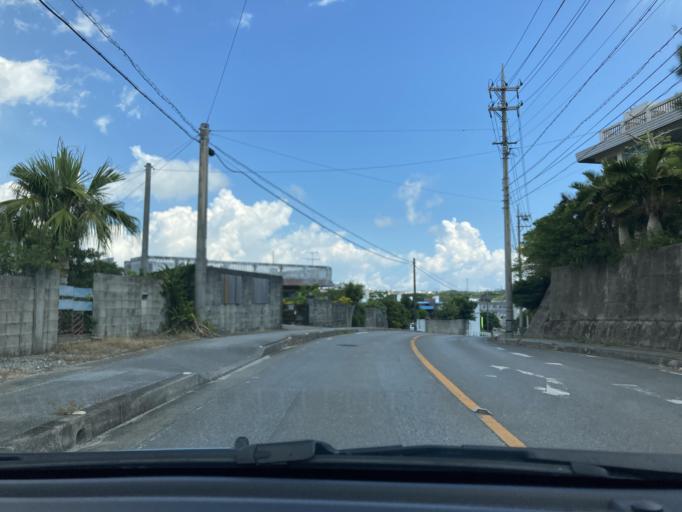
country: JP
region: Okinawa
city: Tomigusuku
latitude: 26.1488
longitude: 127.7909
